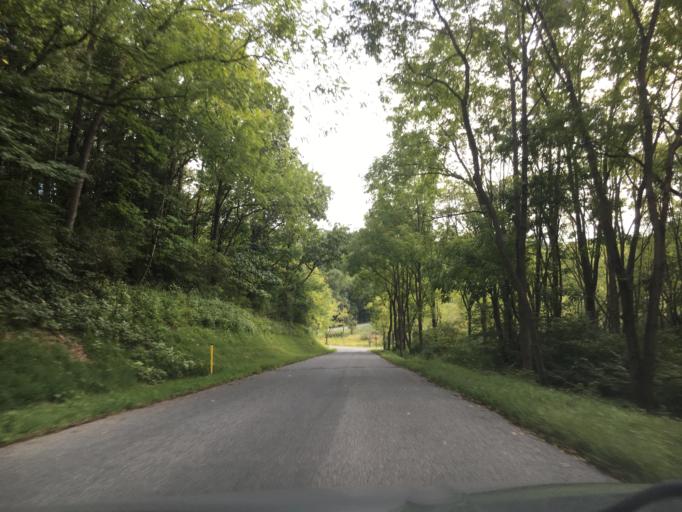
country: US
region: Pennsylvania
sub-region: Berks County
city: Topton
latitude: 40.6098
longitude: -75.7152
